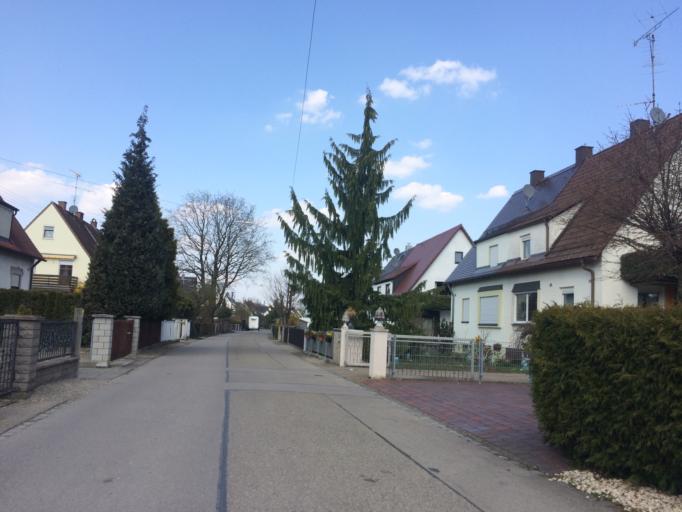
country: DE
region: Bavaria
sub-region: Swabia
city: Augsburg
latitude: 48.4016
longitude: 10.8959
